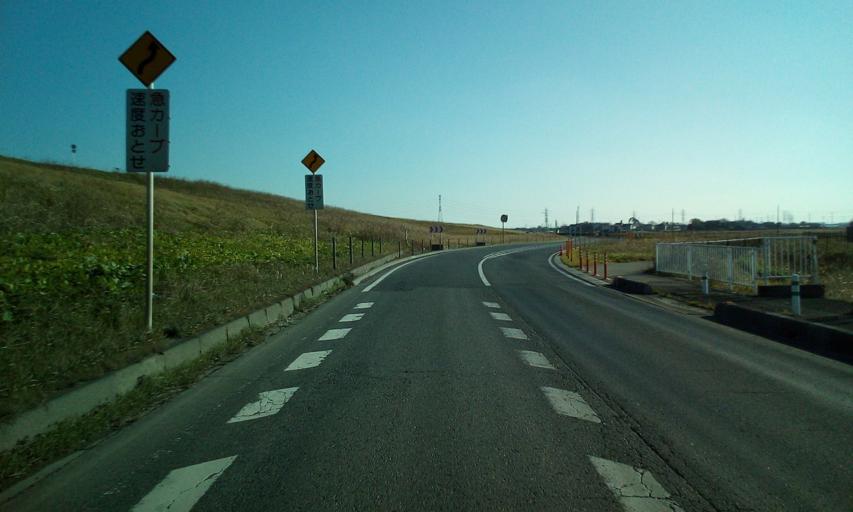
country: JP
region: Chiba
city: Noda
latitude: 35.9240
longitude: 139.8634
